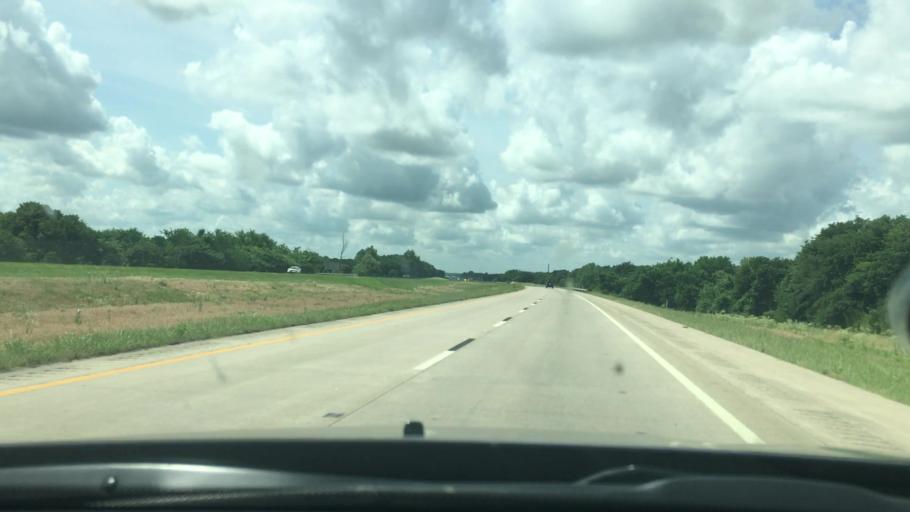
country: US
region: Oklahoma
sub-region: Love County
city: Marietta
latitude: 33.8097
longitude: -97.1346
